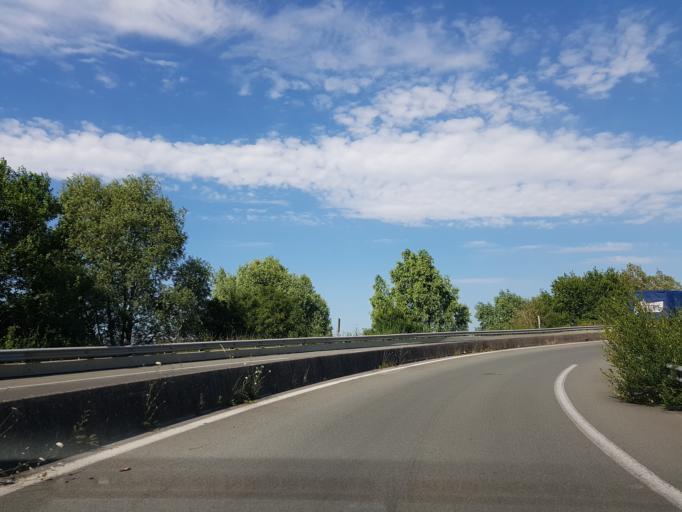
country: FR
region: Nord-Pas-de-Calais
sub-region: Departement du Nord
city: Onnaing
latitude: 50.3684
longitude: 3.5964
